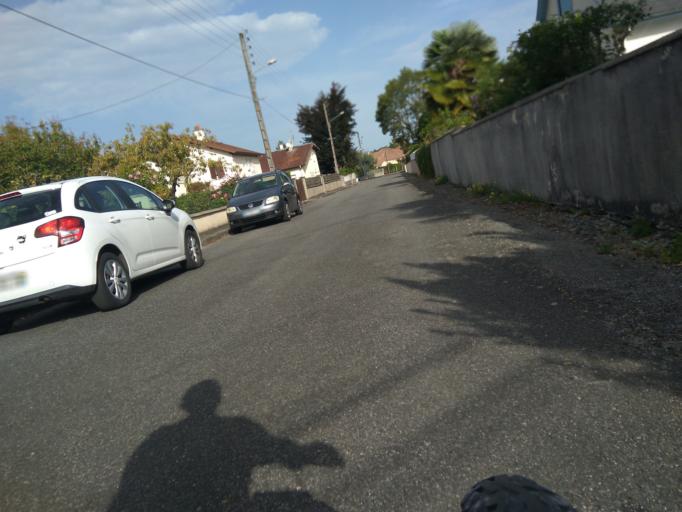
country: FR
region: Aquitaine
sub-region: Departement des Pyrenees-Atlantiques
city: Mazeres-Lezons
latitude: 43.2710
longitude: -0.3423
